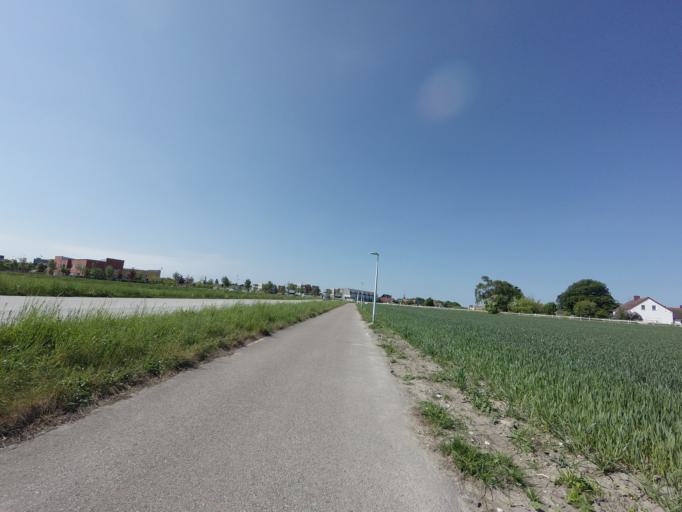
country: SE
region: Skane
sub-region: Vellinge Kommun
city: Hollviken
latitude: 55.4283
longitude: 12.9764
